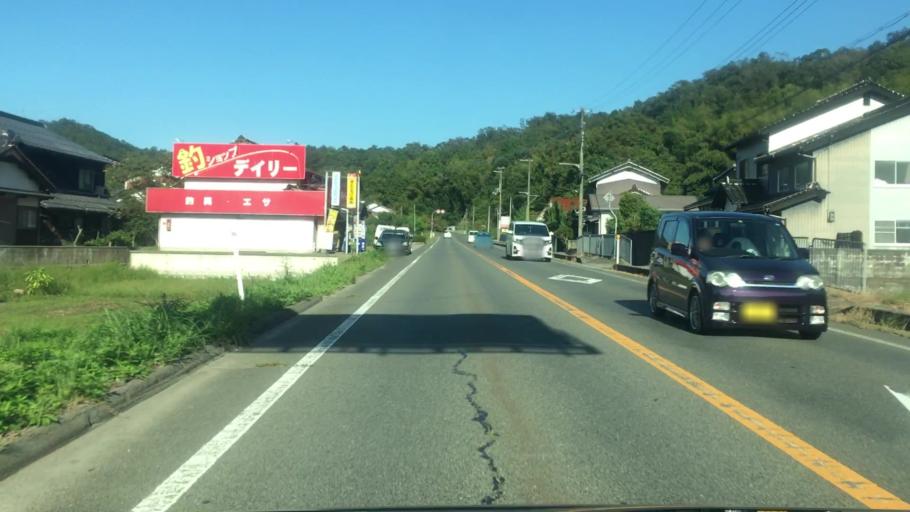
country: JP
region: Hyogo
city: Toyooka
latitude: 35.5573
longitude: 134.8472
